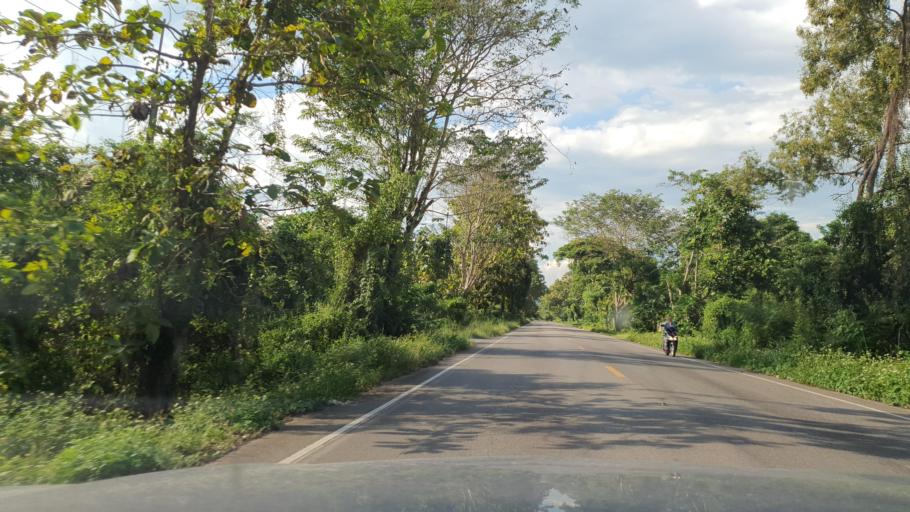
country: TH
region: Phayao
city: Phayao
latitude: 19.1361
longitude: 99.8385
